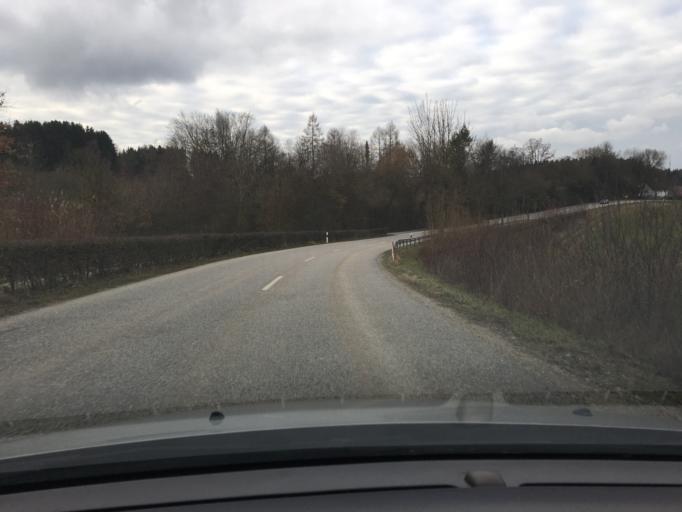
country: DE
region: Bavaria
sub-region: Lower Bavaria
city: Kumhausen
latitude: 48.4936
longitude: 12.1787
